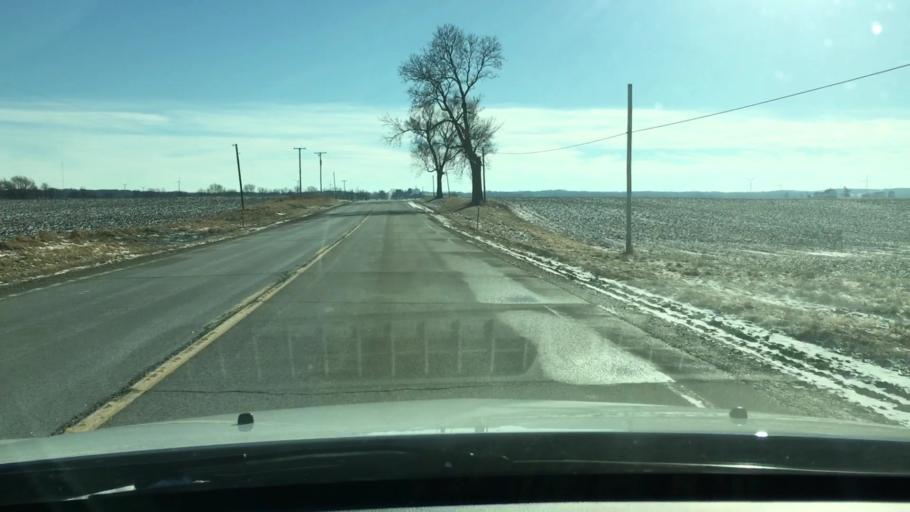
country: US
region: Illinois
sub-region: Ogle County
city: Rochelle
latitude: 41.7557
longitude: -89.0837
